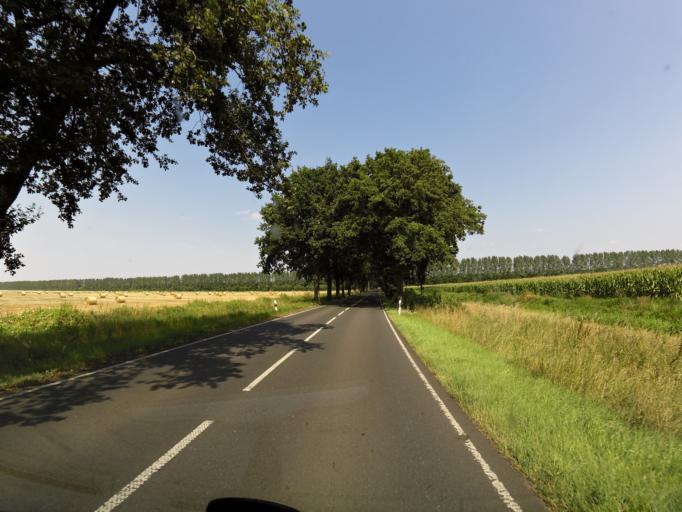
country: DE
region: Brandenburg
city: Liebenwalde
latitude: 52.8645
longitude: 13.3319
